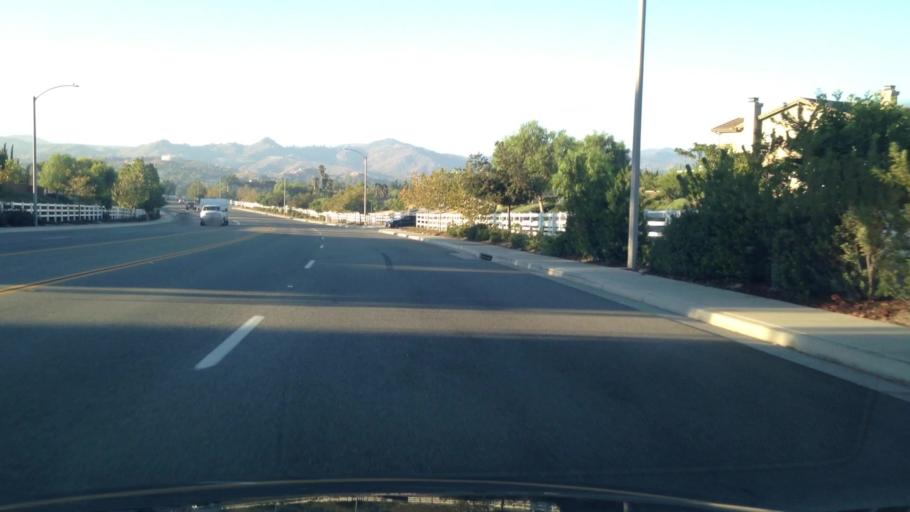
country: US
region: California
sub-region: Riverside County
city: Woodcrest
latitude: 33.8636
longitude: -117.3667
